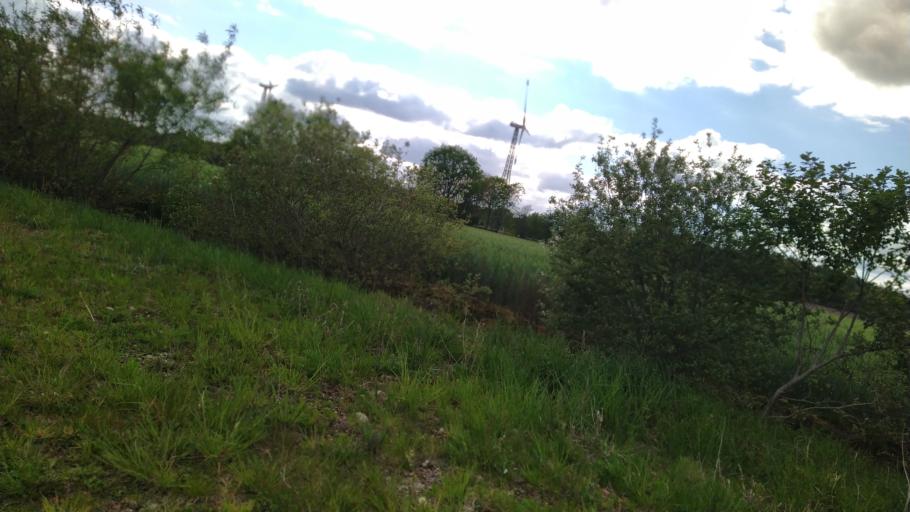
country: DE
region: Lower Saxony
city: Brest
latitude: 53.4406
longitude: 9.3942
